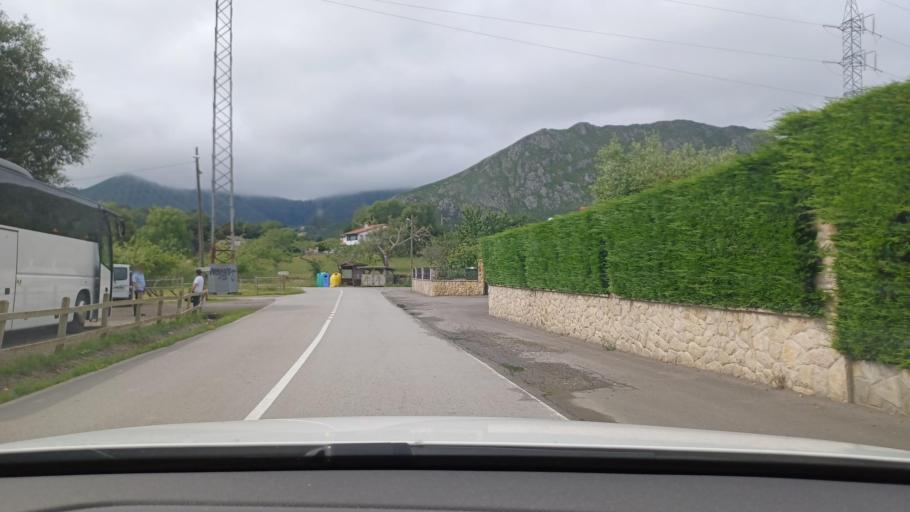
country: ES
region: Asturias
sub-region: Province of Asturias
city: Ribadesella
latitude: 43.4561
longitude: -5.1183
